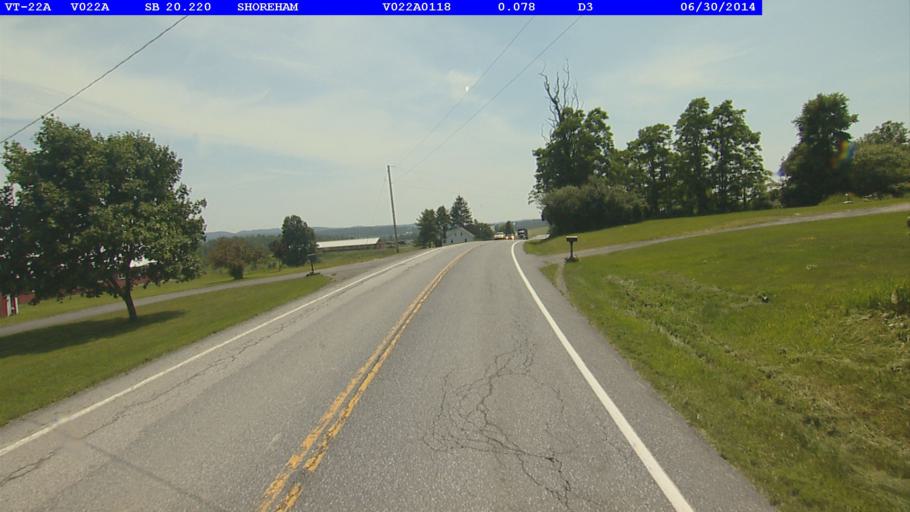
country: US
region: New York
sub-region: Essex County
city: Ticonderoga
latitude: 43.8506
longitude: -73.3091
